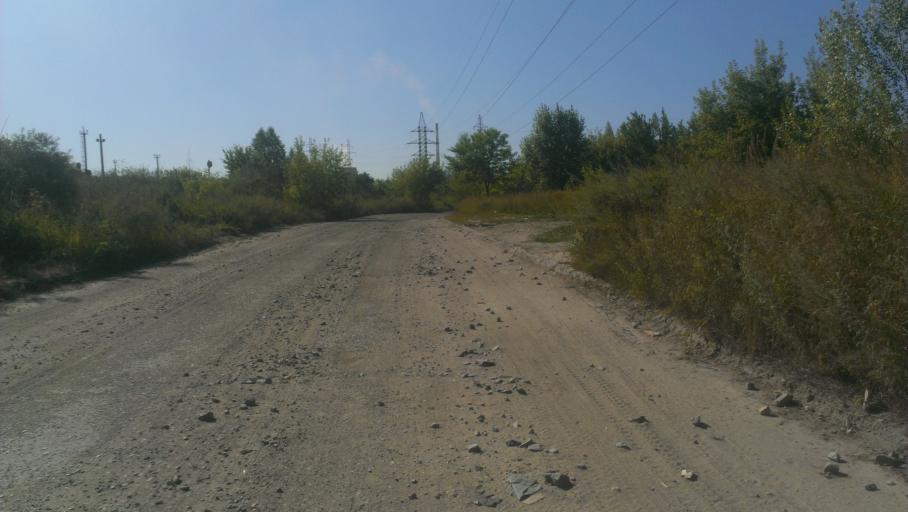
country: RU
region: Altai Krai
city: Novosilikatnyy
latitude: 53.3277
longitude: 83.6444
